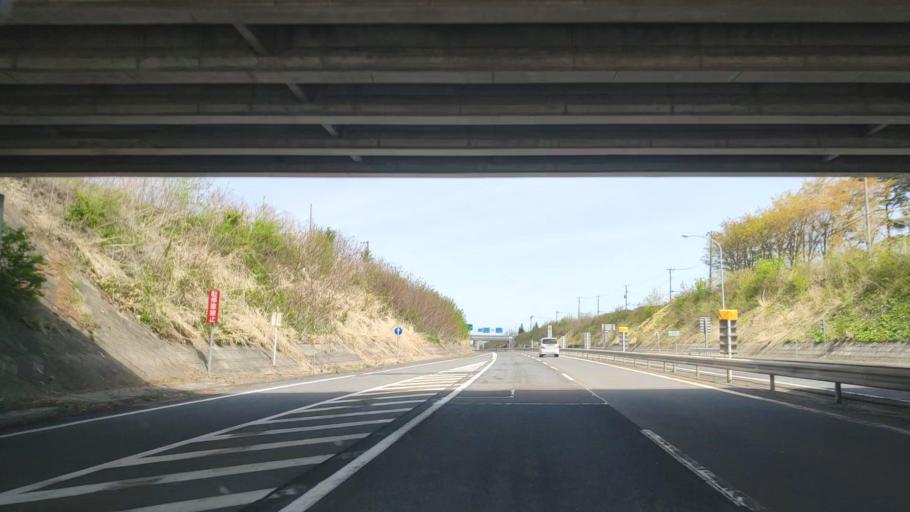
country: JP
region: Aomori
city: Hachinohe
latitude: 40.4874
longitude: 141.4632
